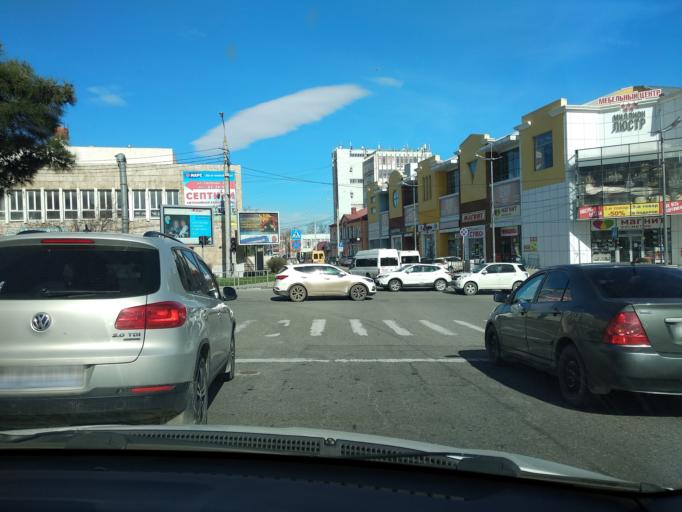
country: RU
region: Krasnodarskiy
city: Novorossiysk
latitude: 44.7194
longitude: 37.7694
